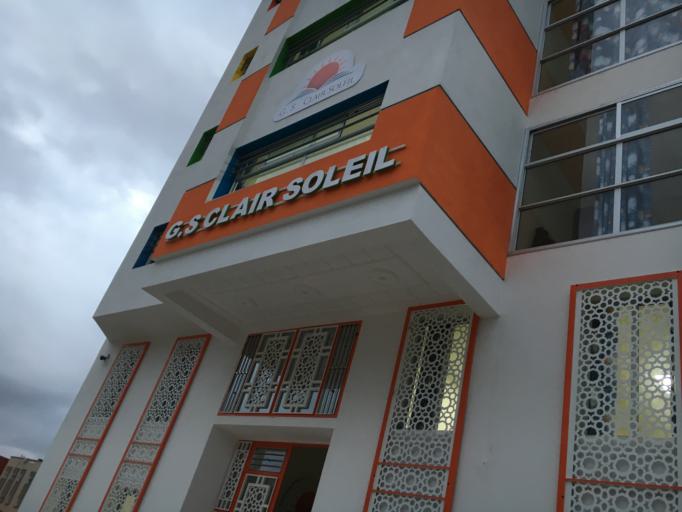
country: MA
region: Fes-Boulemane
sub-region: Fes
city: Fes
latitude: 34.0557
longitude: -5.0390
